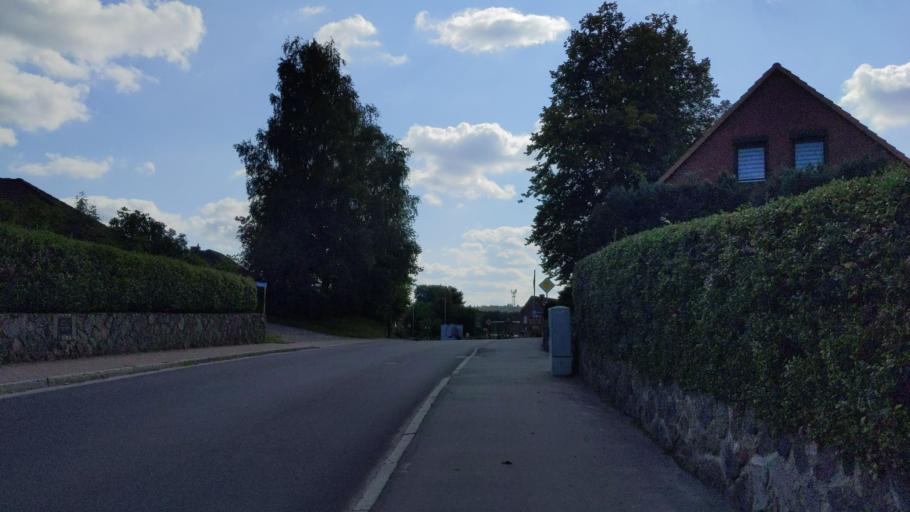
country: DE
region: Schleswig-Holstein
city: Kasseedorf
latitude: 54.1651
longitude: 10.7221
